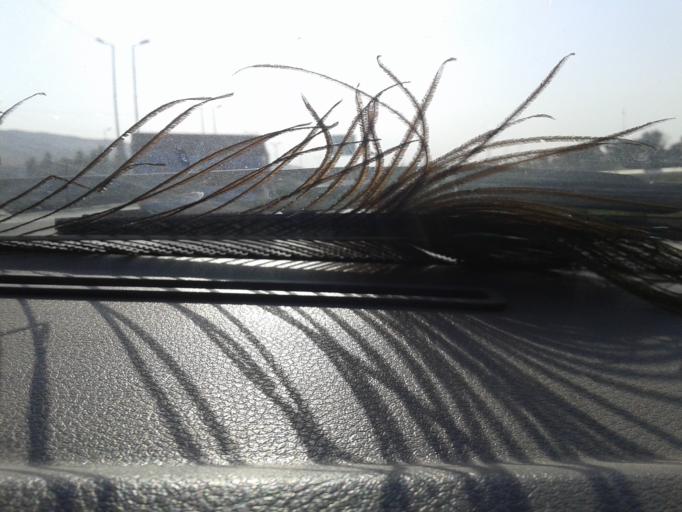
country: IR
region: Tehran
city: Tehran
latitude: 35.7240
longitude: 51.5849
